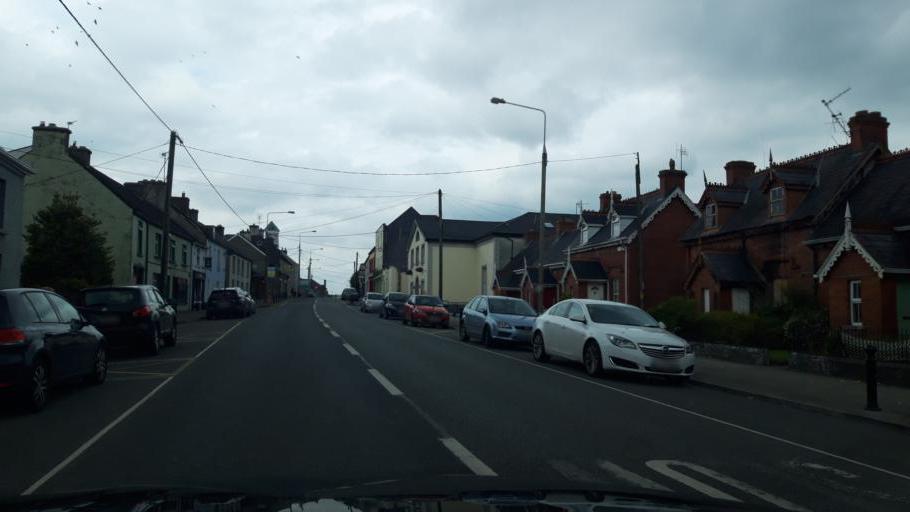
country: IE
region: Leinster
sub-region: Kilkenny
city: Castlecomer
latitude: 52.8035
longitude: -7.2103
